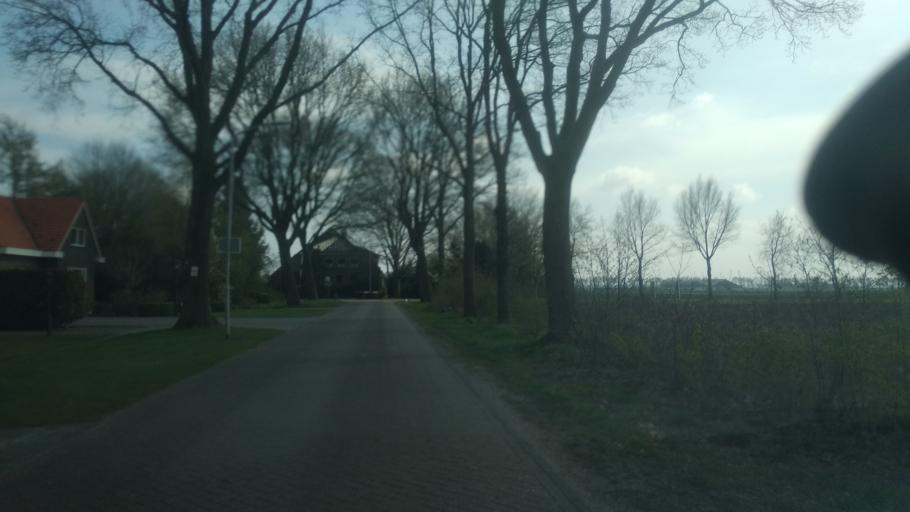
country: NL
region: Groningen
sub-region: Gemeente Stadskanaal
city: Stadskanaal
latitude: 52.9928
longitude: 6.9277
